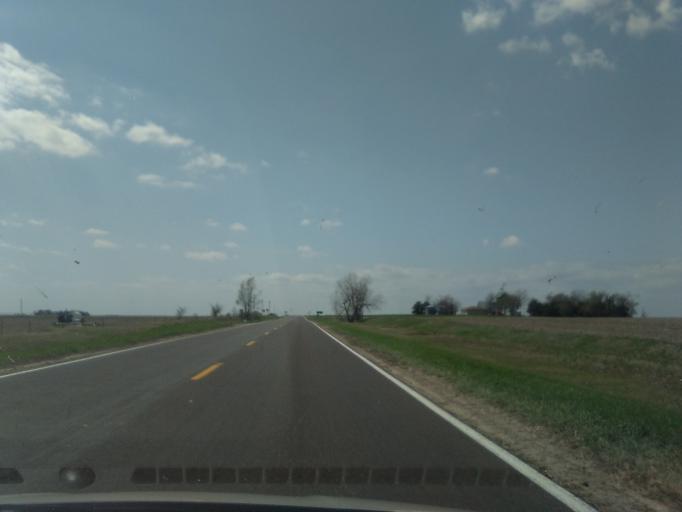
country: US
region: Nebraska
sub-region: Thayer County
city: Hebron
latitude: 40.3212
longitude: -97.4605
